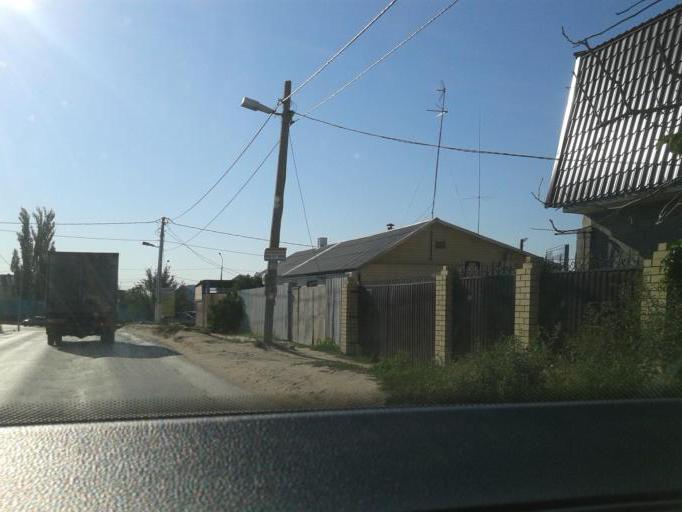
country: RU
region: Volgograd
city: Volgograd
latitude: 48.6902
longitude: 44.4575
